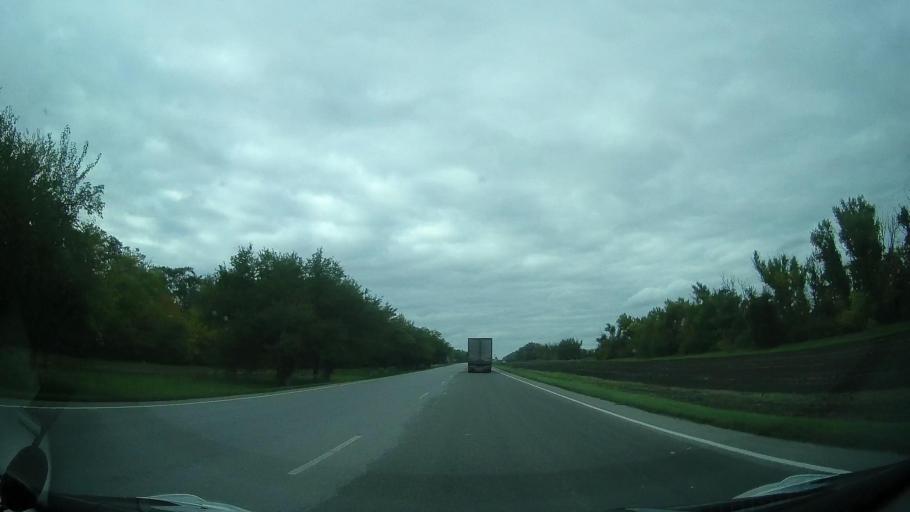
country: RU
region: Rostov
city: Yegorlykskaya
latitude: 46.6220
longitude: 40.5961
